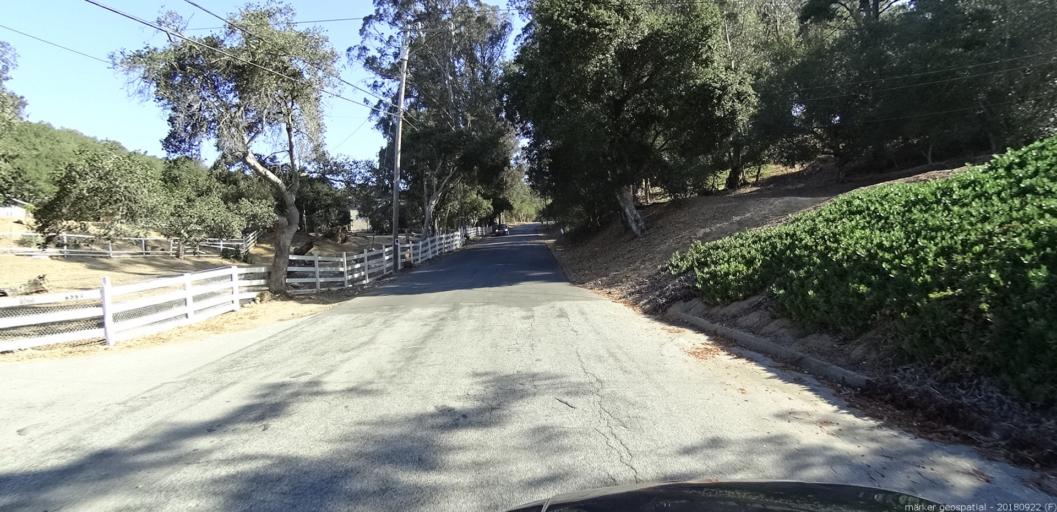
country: US
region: California
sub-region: Monterey County
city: Prunedale
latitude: 36.8229
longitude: -121.6429
